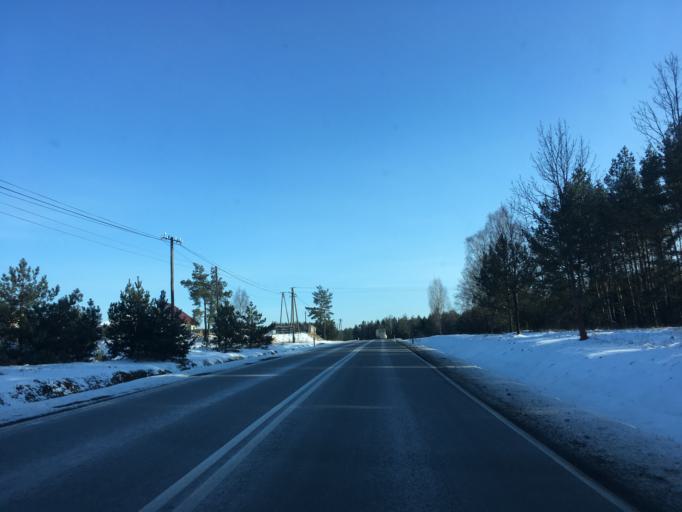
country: PL
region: Pomeranian Voivodeship
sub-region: Powiat koscierski
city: Lipusz
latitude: 54.1287
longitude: 17.8714
